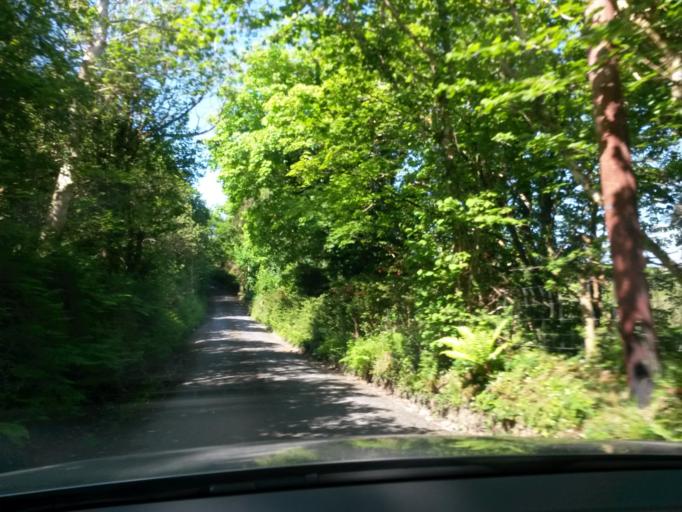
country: IE
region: Munster
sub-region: Ciarrai
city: Cahersiveen
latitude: 51.7337
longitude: -9.9579
